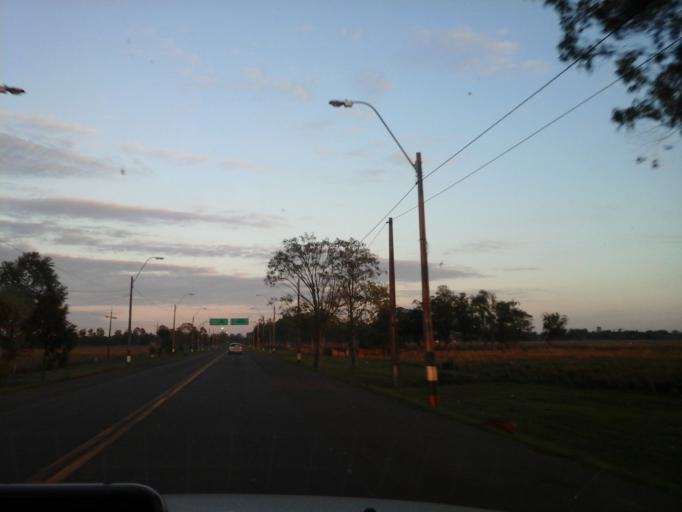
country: PY
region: Itapua
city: General Delgado
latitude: -27.0880
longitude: -56.5300
